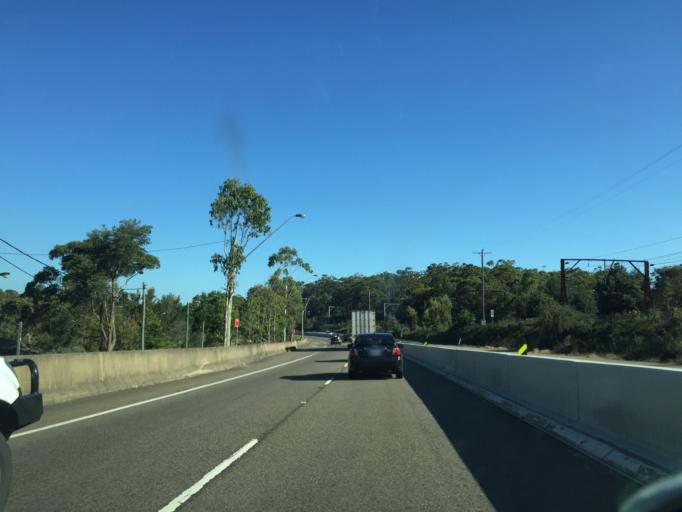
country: AU
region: New South Wales
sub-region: Blue Mountains Municipality
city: Blaxland
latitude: -33.7186
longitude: 150.5931
